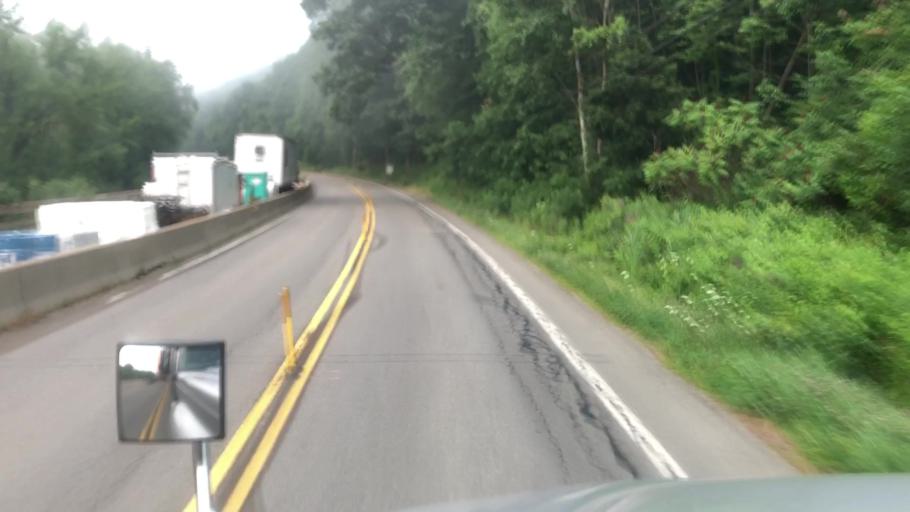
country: US
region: Pennsylvania
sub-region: Venango County
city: Oil City
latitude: 41.4267
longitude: -79.7271
